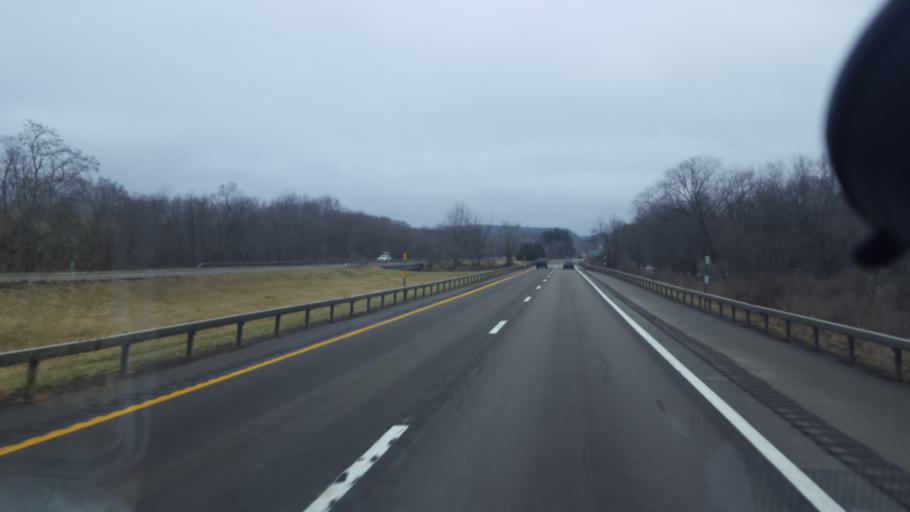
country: US
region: New York
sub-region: Chautauqua County
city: Falconer
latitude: 42.1403
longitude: -79.1058
